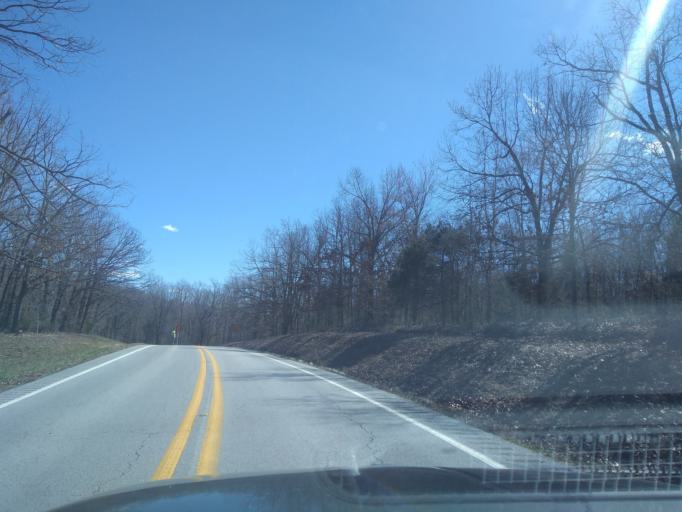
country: US
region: Arkansas
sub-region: Washington County
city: Farmington
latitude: 36.0848
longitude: -94.3258
